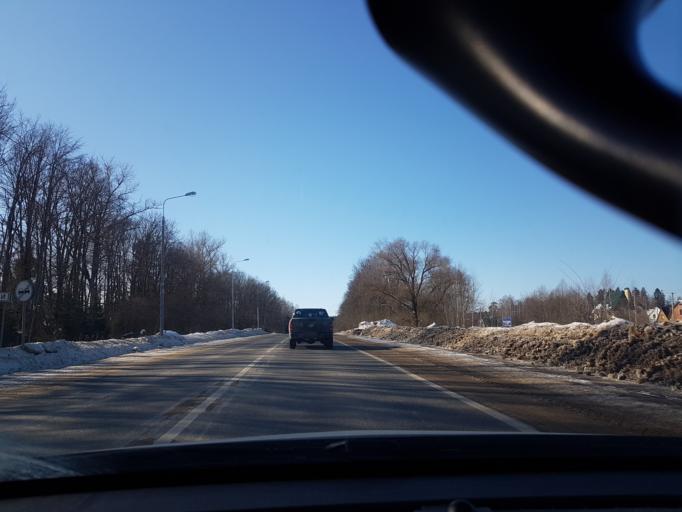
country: RU
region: Moskovskaya
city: Kostrovo
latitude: 55.9177
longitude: 36.6771
